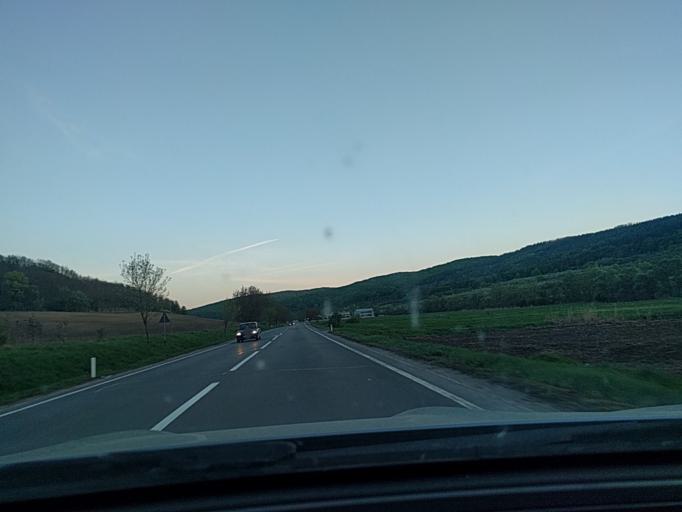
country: RO
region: Mures
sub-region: Comuna Nades
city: Nades
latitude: 46.3375
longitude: 24.7107
